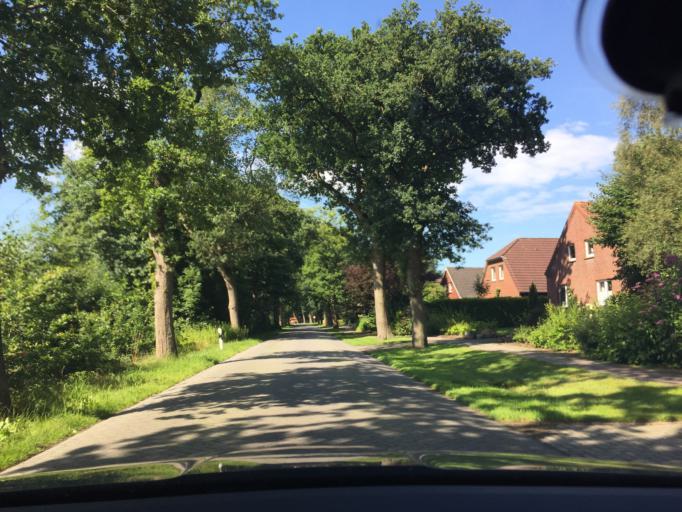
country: DE
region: Lower Saxony
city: Rechtsupweg
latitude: 53.5025
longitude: 7.3397
